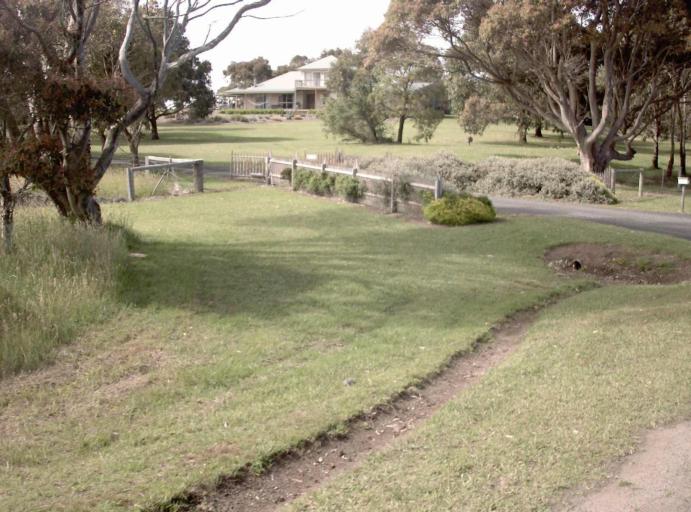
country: AU
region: Victoria
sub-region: Bass Coast
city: Phillip Island
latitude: -38.4798
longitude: 145.1788
